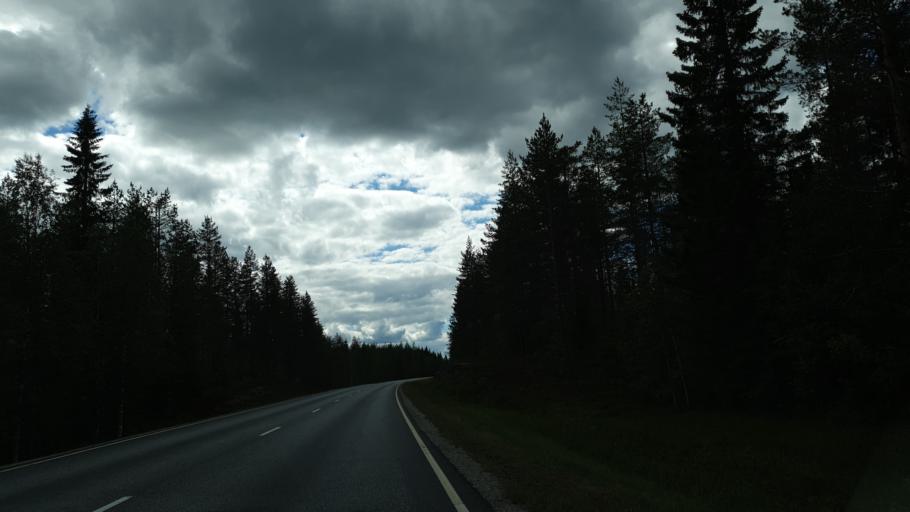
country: FI
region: Kainuu
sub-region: Kehys-Kainuu
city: Kuhmo
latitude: 63.8640
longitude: 29.4812
